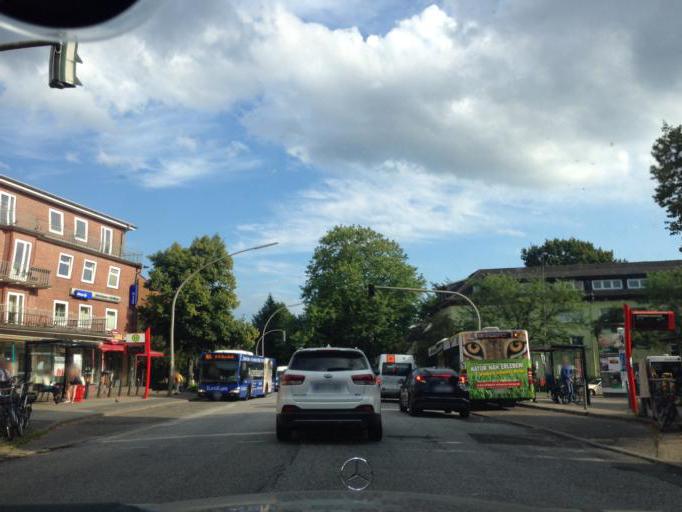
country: DE
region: Hamburg
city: Steilshoop
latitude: 53.5925
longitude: 10.0755
